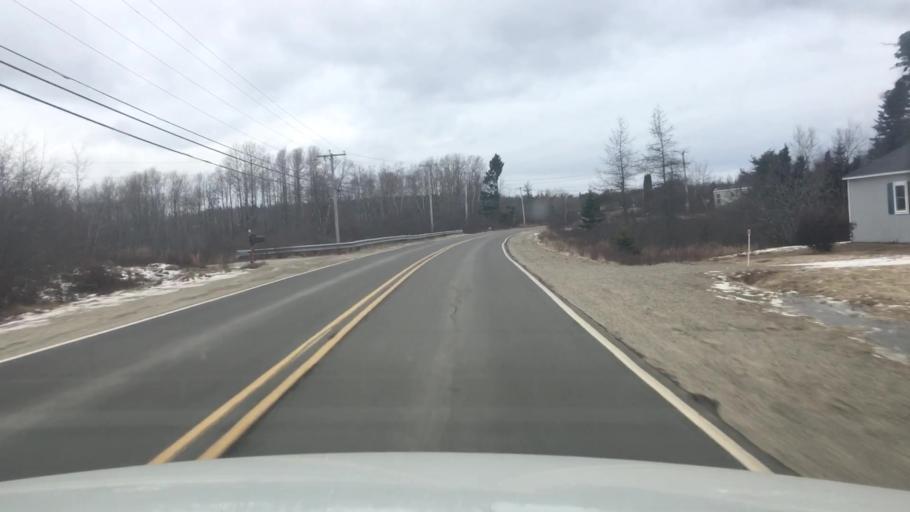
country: US
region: Maine
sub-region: Washington County
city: Jonesport
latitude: 44.5526
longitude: -67.6240
